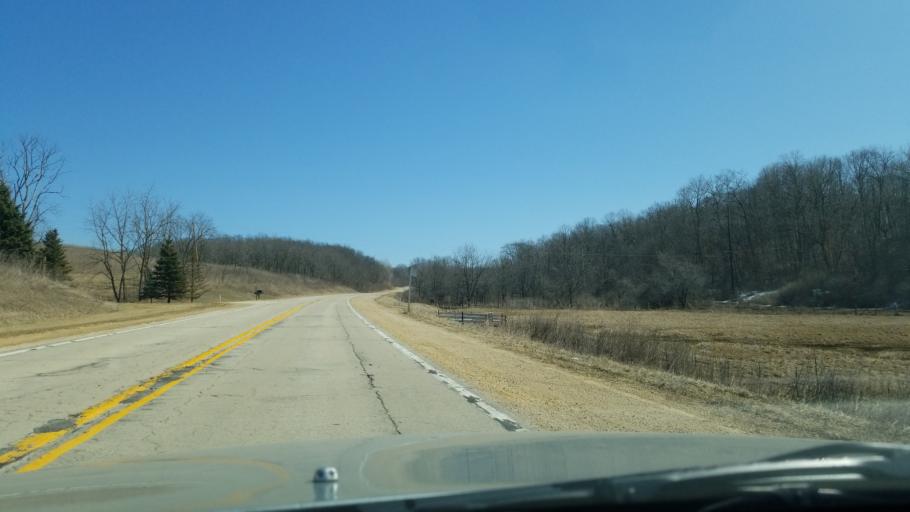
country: US
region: Wisconsin
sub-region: Iowa County
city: Mineral Point
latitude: 42.9058
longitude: -90.2356
